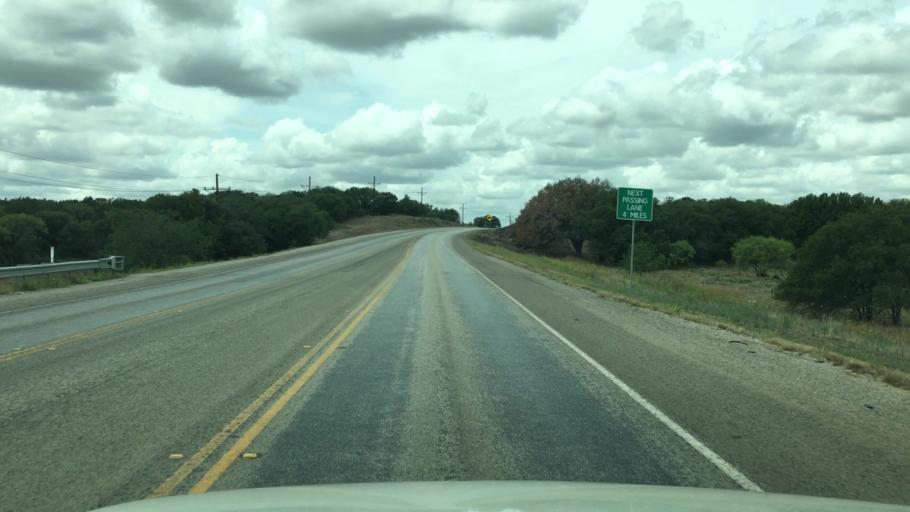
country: US
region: Texas
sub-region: McCulloch County
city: Brady
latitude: 31.0036
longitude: -99.1962
